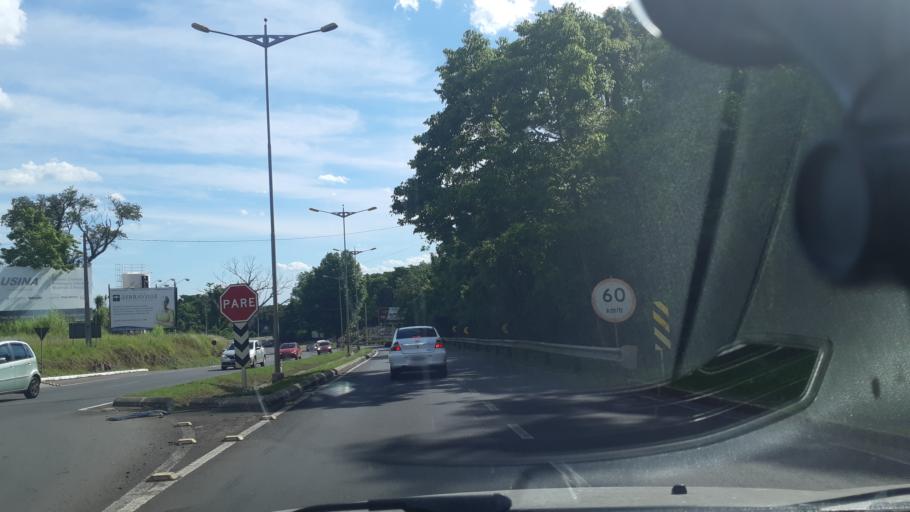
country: BR
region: Rio Grande do Sul
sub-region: Ivoti
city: Ivoti
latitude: -29.6259
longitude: -51.1371
